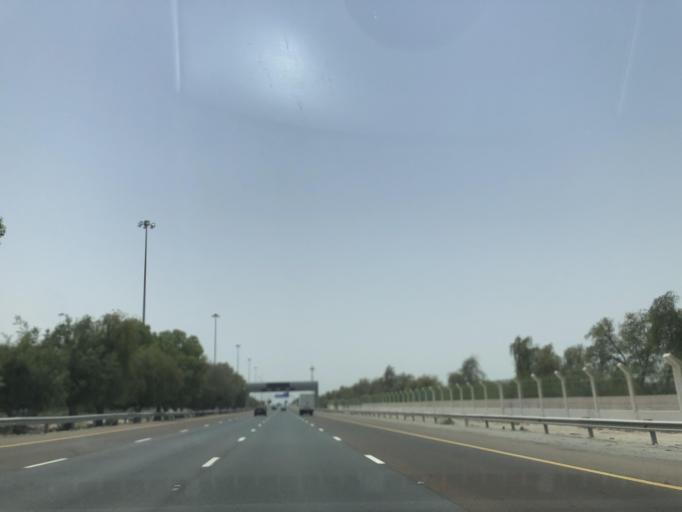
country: AE
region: Abu Dhabi
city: Abu Dhabi
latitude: 24.7128
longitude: 54.7960
